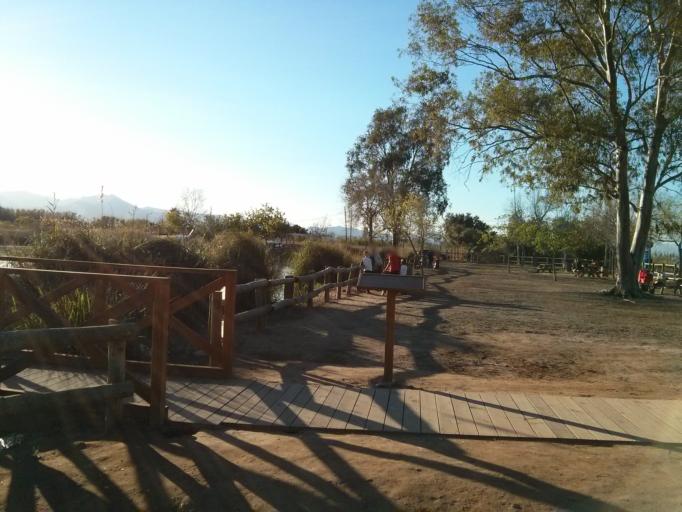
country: ES
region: Valencia
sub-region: Provincia de Castello
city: Moncofar
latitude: 39.8332
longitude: -0.1063
